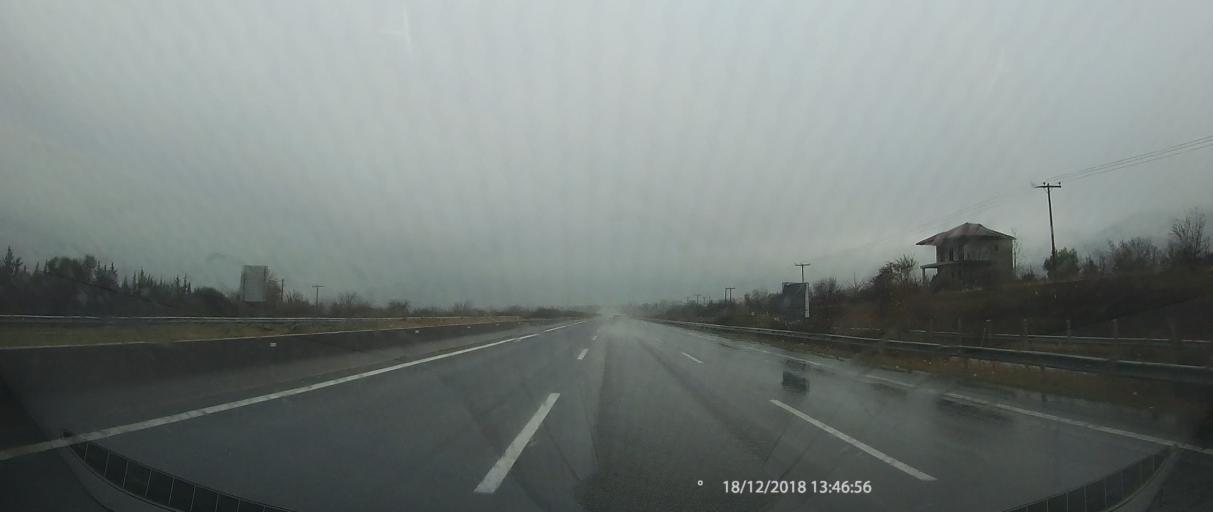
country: GR
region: Central Macedonia
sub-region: Nomos Pierias
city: Leptokarya
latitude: 40.0876
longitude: 22.5551
